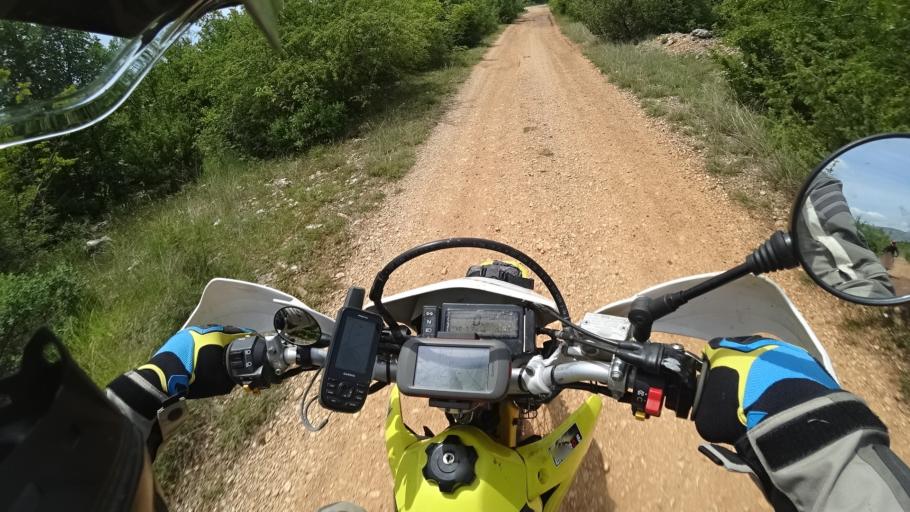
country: HR
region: Sibensko-Kniniska
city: Kistanje
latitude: 44.0596
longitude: 16.0572
